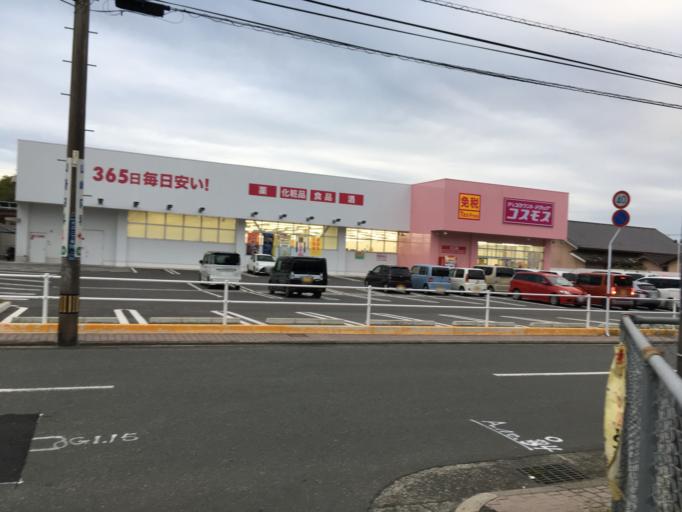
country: JP
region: Kumamoto
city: Kumamoto
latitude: 32.8052
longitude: 130.7343
